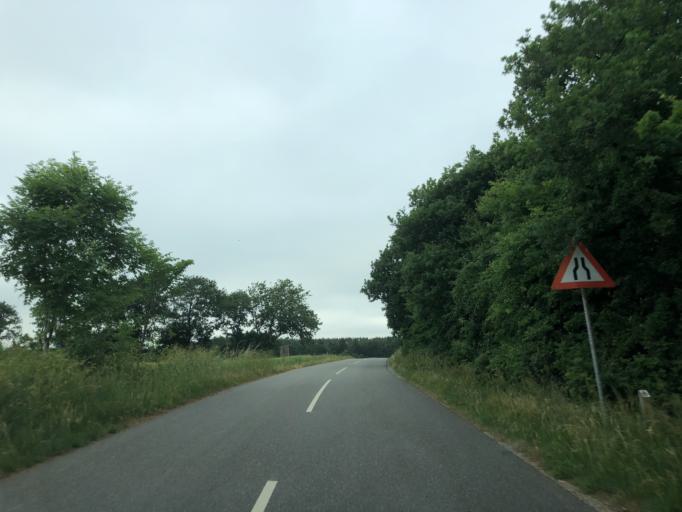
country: DK
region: Central Jutland
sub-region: Holstebro Kommune
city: Holstebro
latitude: 56.2581
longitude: 8.6325
